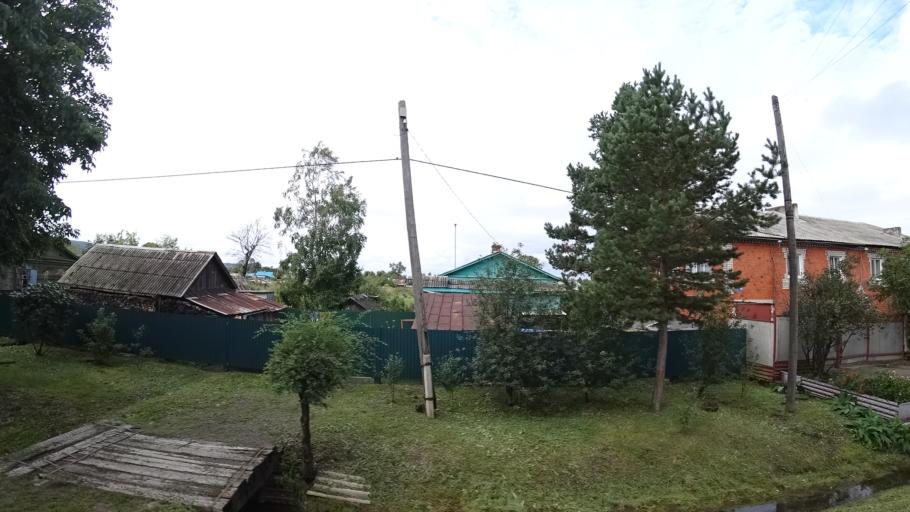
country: RU
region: Primorskiy
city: Chernigovka
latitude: 44.3424
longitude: 132.5679
